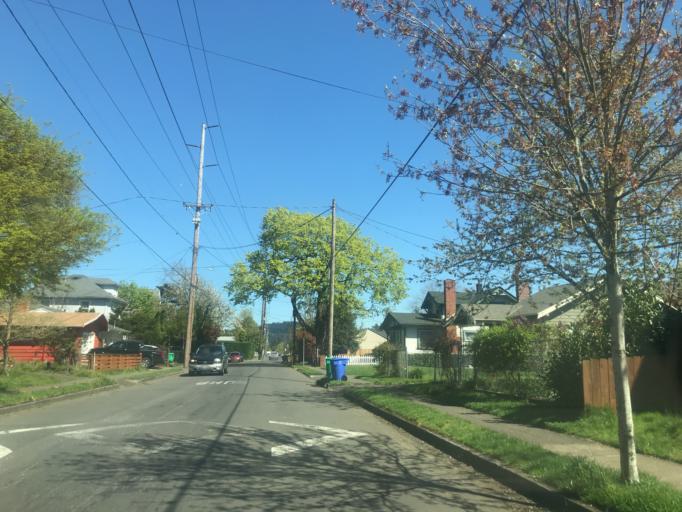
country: US
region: Oregon
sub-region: Multnomah County
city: Lents
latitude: 45.4854
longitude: -122.5945
